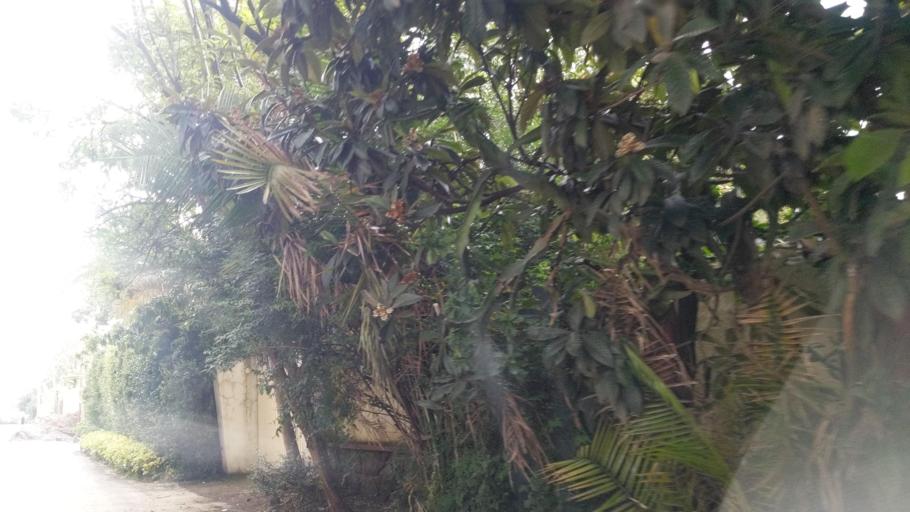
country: ET
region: Adis Abeba
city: Addis Ababa
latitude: 8.9964
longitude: 38.7807
